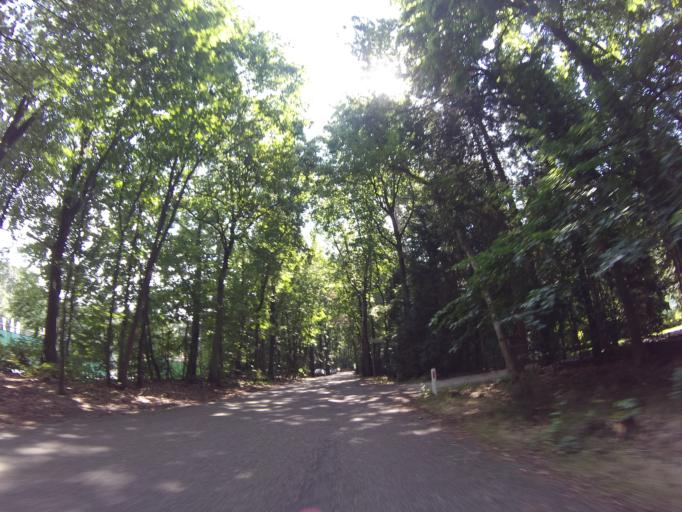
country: NL
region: Utrecht
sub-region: Gemeente Zeist
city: Zeist
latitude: 52.1190
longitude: 5.2437
